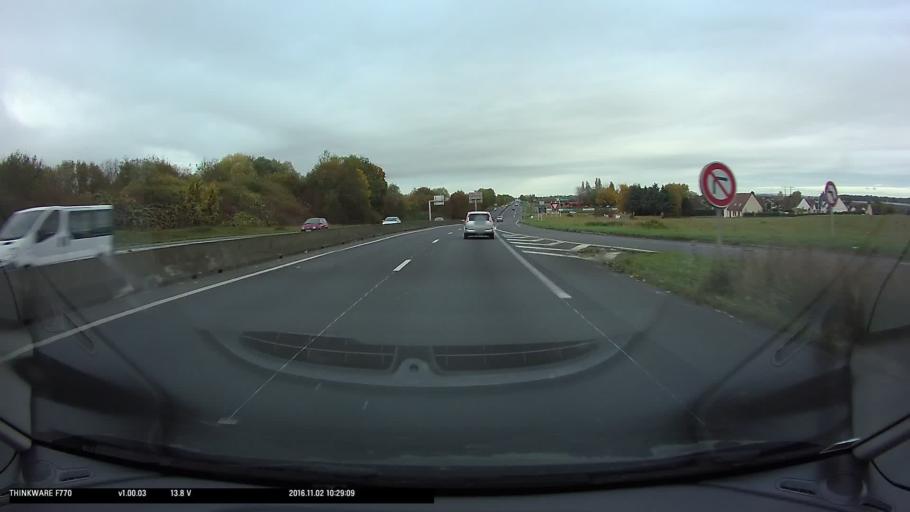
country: FR
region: Ile-de-France
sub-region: Departement du Val-d'Oise
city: Courdimanche
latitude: 49.0580
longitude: 2.0047
